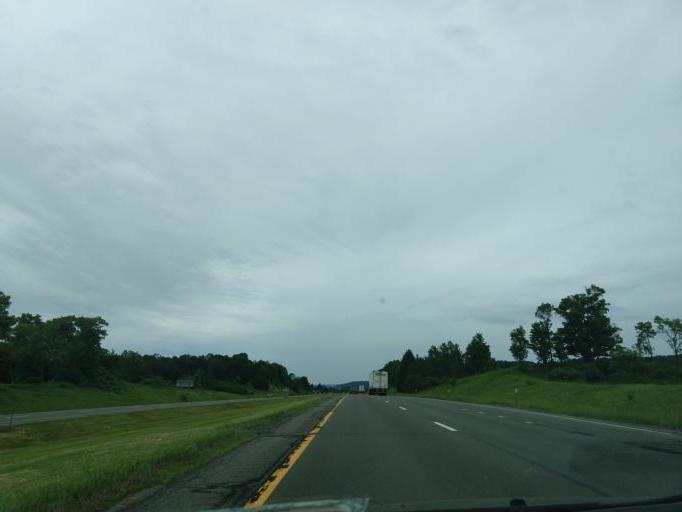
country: US
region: New York
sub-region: Chenango County
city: Lakeview
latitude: 42.3187
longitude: -75.9660
